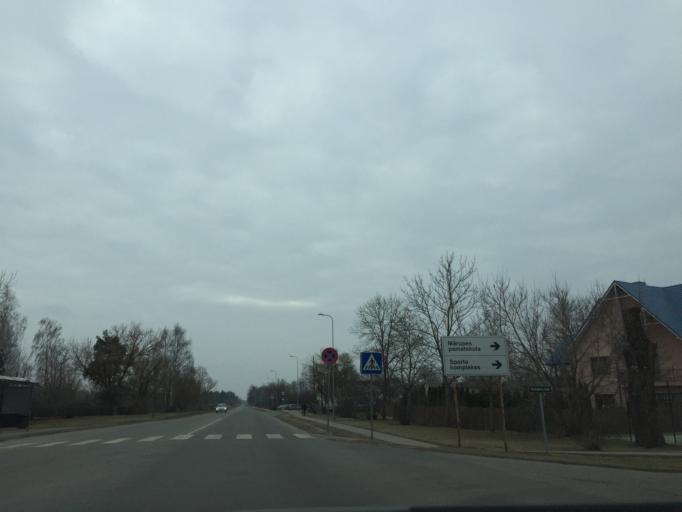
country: LV
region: Marupe
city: Marupe
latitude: 56.8835
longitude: 24.0694
